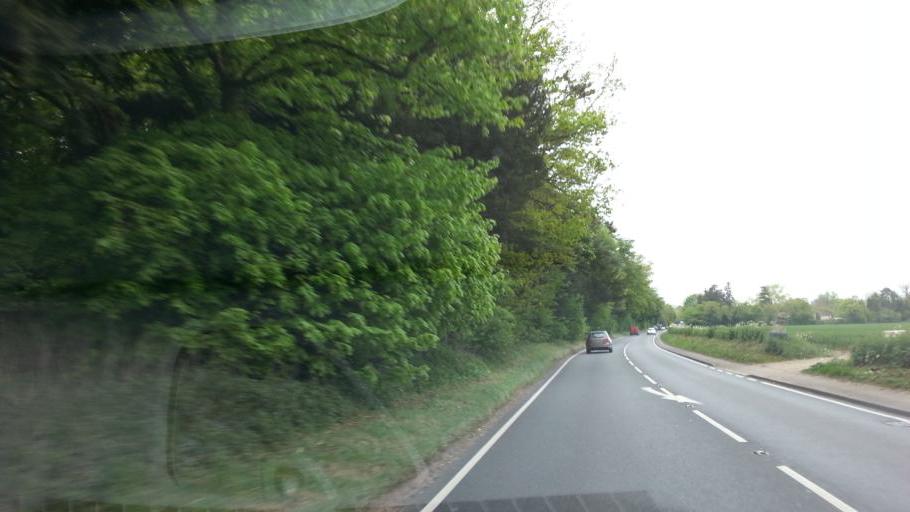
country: GB
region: England
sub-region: Suffolk
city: Bury St Edmunds
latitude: 52.2256
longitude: 0.7344
